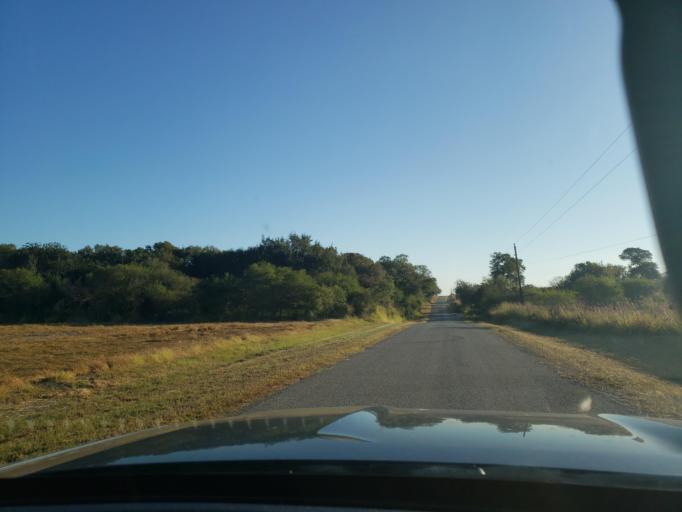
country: US
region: Texas
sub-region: Bee County
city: Beeville
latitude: 28.4237
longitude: -97.7053
